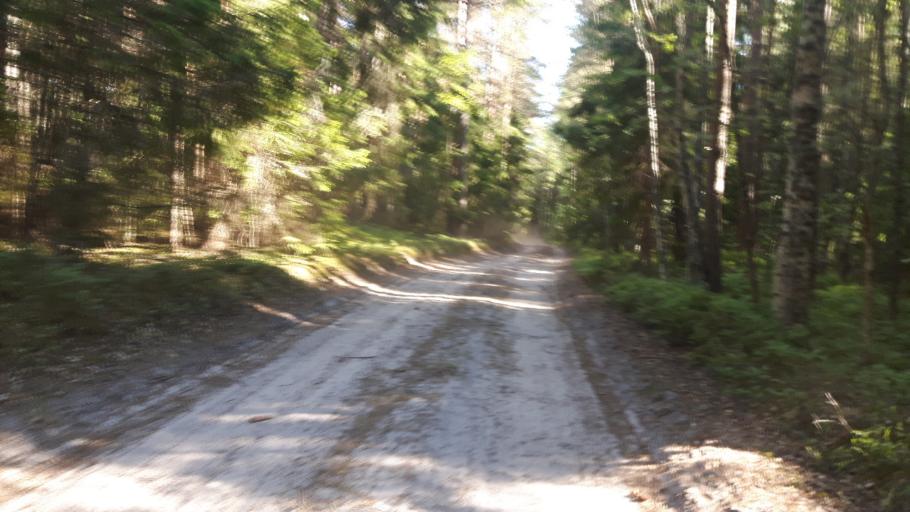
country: LV
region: Salacgrivas
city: Salacgriva
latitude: 57.7201
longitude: 24.3477
